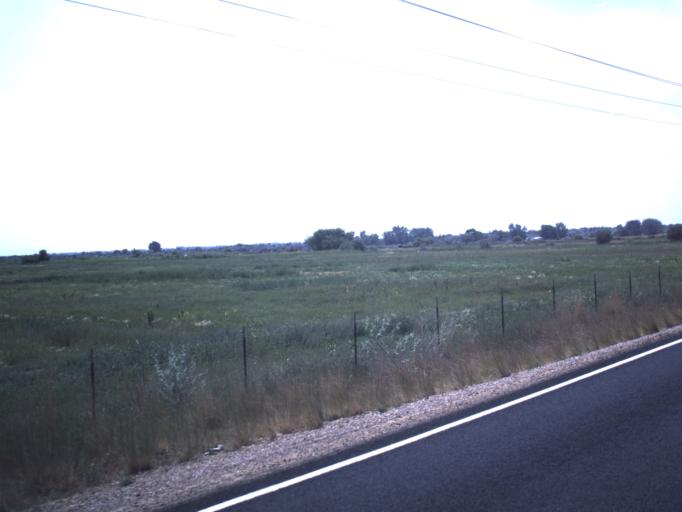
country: US
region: Utah
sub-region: Duchesne County
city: Roosevelt
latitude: 40.4037
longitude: -109.8475
